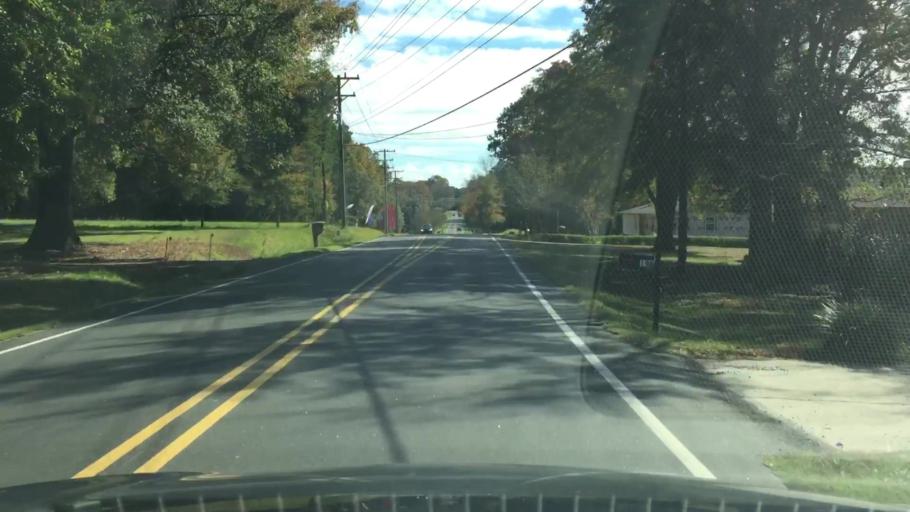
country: US
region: North Carolina
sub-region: Gaston County
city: Davidson
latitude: 35.5418
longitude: -80.8408
